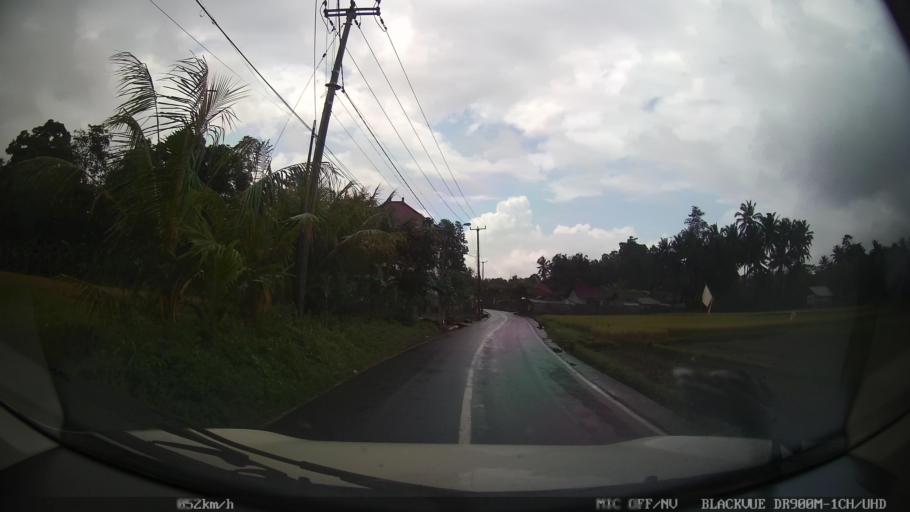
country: ID
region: Bali
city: Banjar Teguan
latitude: -8.5115
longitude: 115.2291
